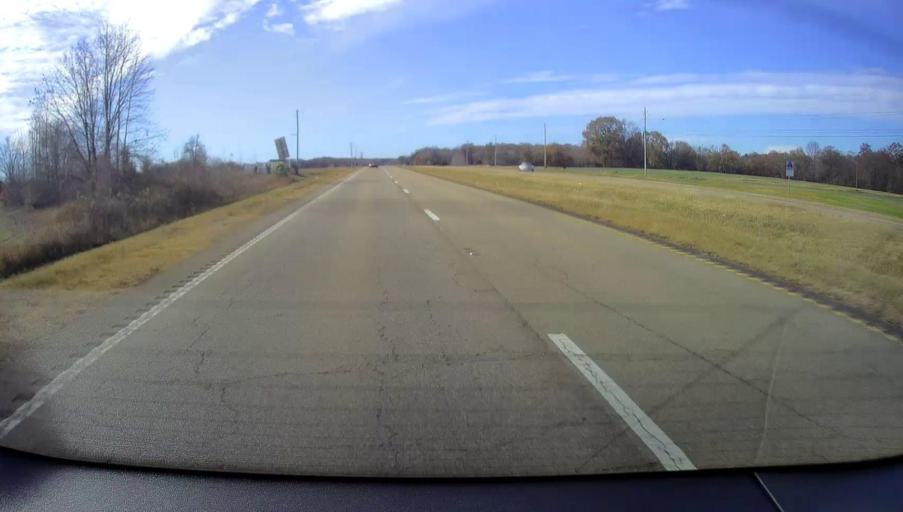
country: US
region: Mississippi
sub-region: Alcorn County
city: Corinth
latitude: 34.9310
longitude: -88.6212
